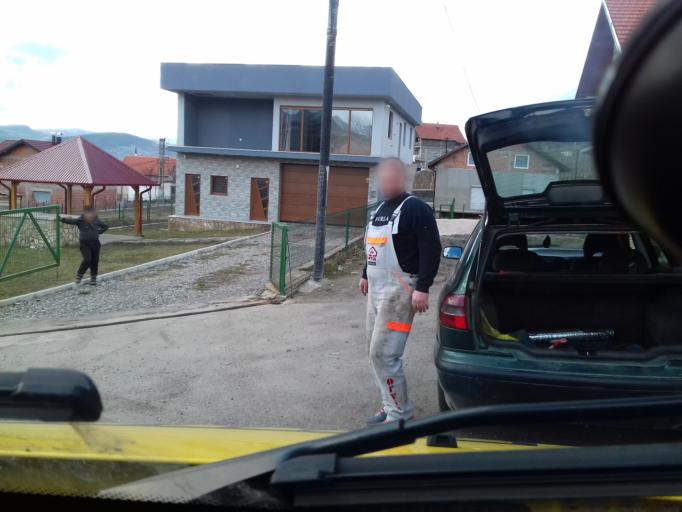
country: BA
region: Federation of Bosnia and Herzegovina
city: Zenica
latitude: 44.1858
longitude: 17.9690
